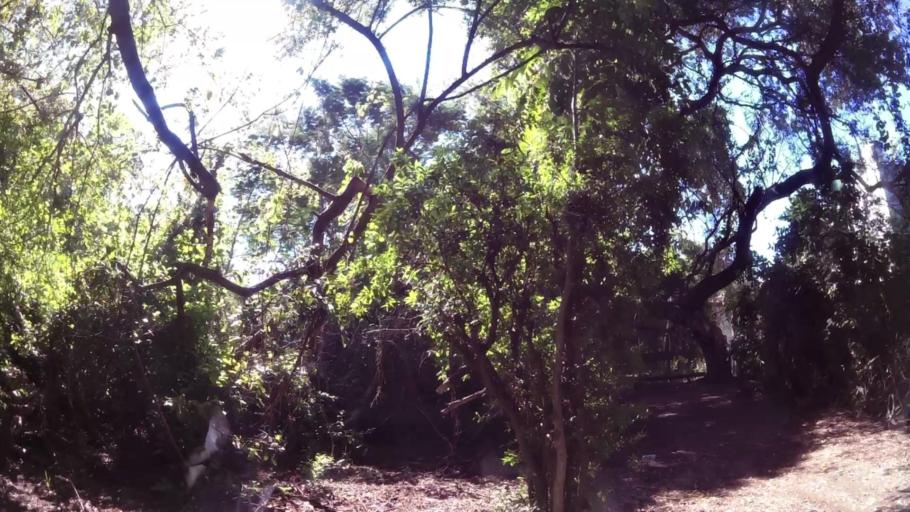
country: GT
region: Santa Rosa
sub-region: Municipio de Taxisco
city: Taxisco
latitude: 13.8906
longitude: -90.4781
